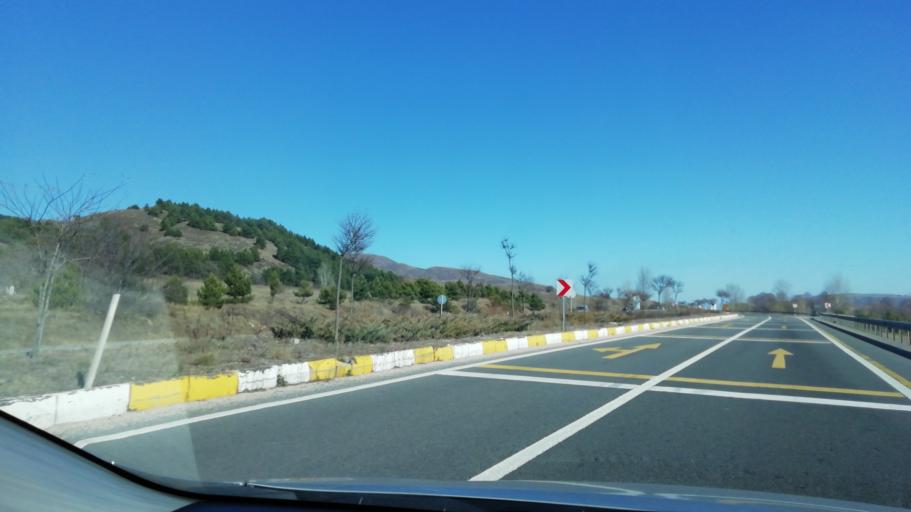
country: TR
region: Karabuk
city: Gozyeri
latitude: 40.8491
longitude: 32.4578
